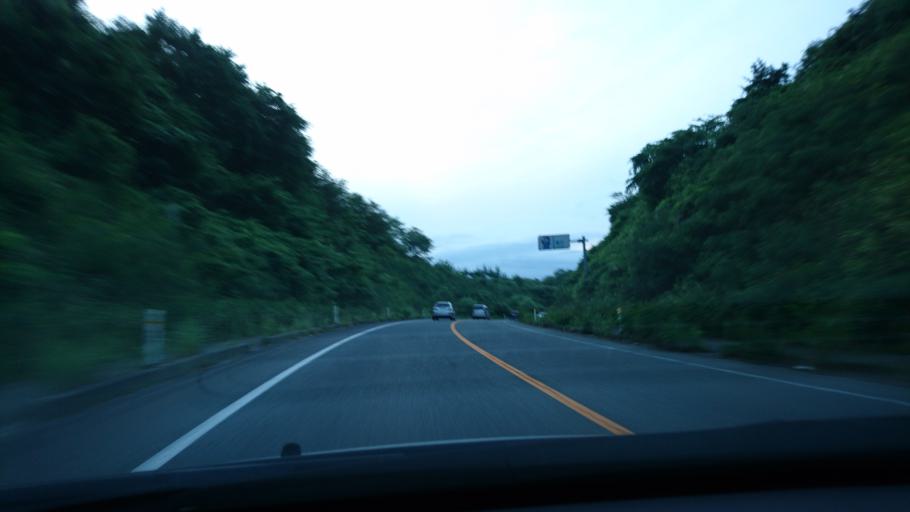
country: JP
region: Iwate
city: Ichinoseki
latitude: 38.7940
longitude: 140.9782
